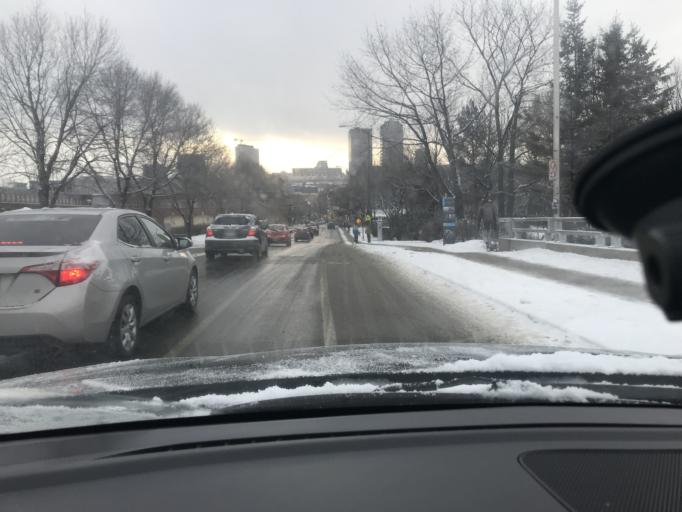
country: CA
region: Quebec
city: Quebec
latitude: 46.8189
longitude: -71.2234
